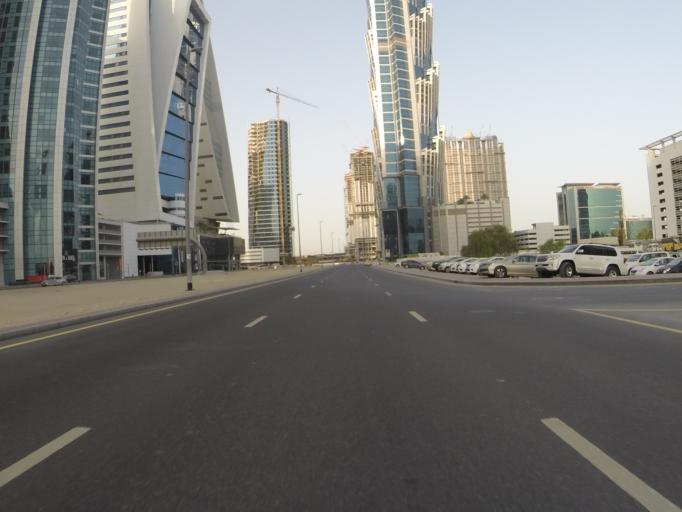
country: AE
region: Dubai
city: Dubai
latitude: 25.1880
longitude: 55.2607
